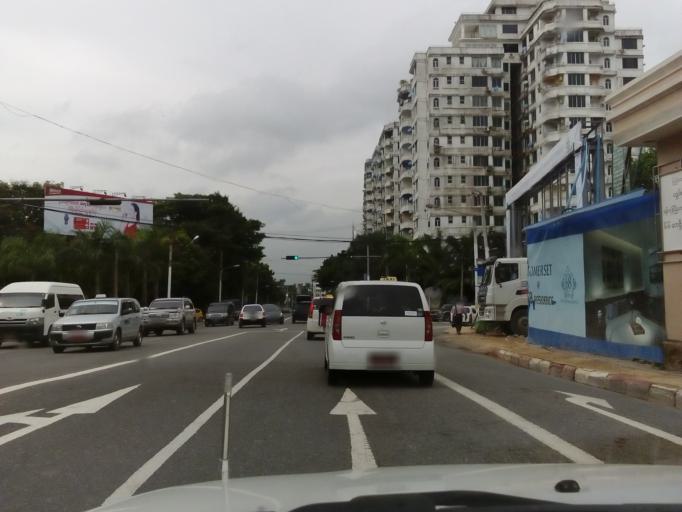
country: MM
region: Yangon
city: Yangon
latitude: 16.8148
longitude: 96.1559
